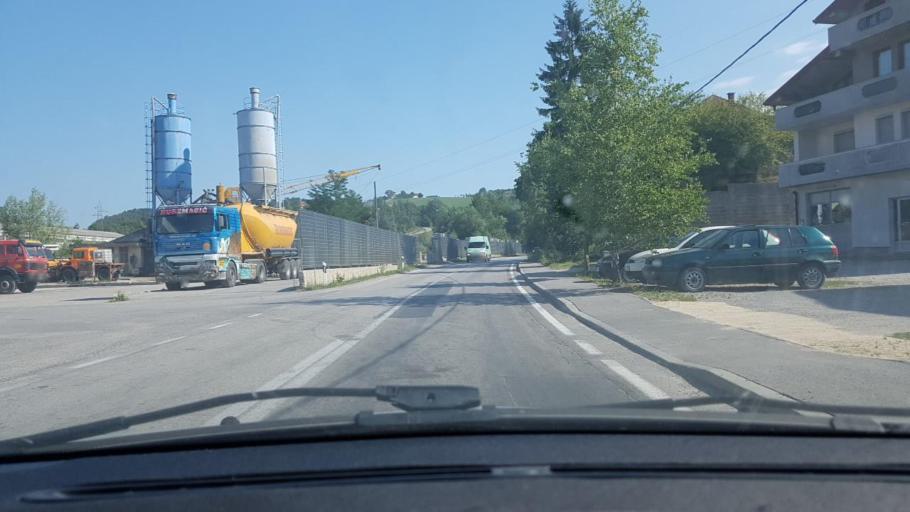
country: BA
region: Federation of Bosnia and Herzegovina
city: Coralici
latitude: 44.9929
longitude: 15.8974
